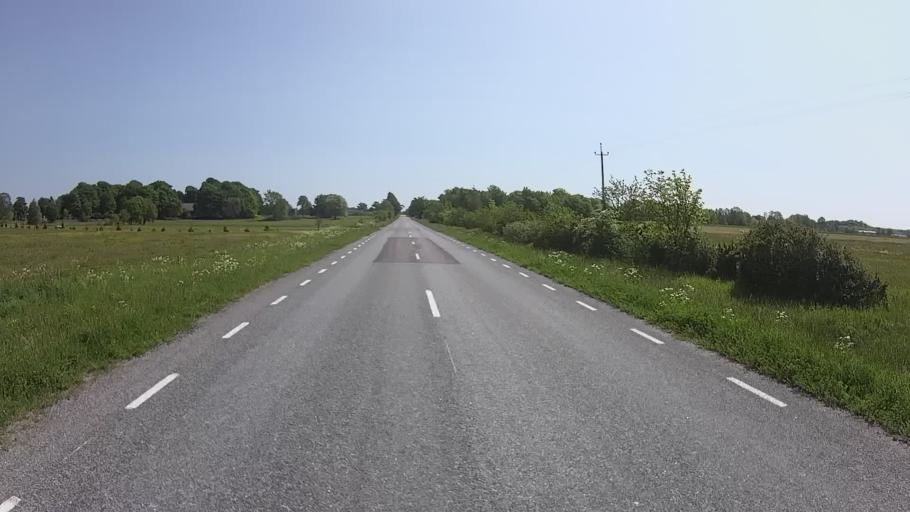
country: EE
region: Saare
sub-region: Kuressaare linn
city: Kuressaare
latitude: 58.3695
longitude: 22.0481
